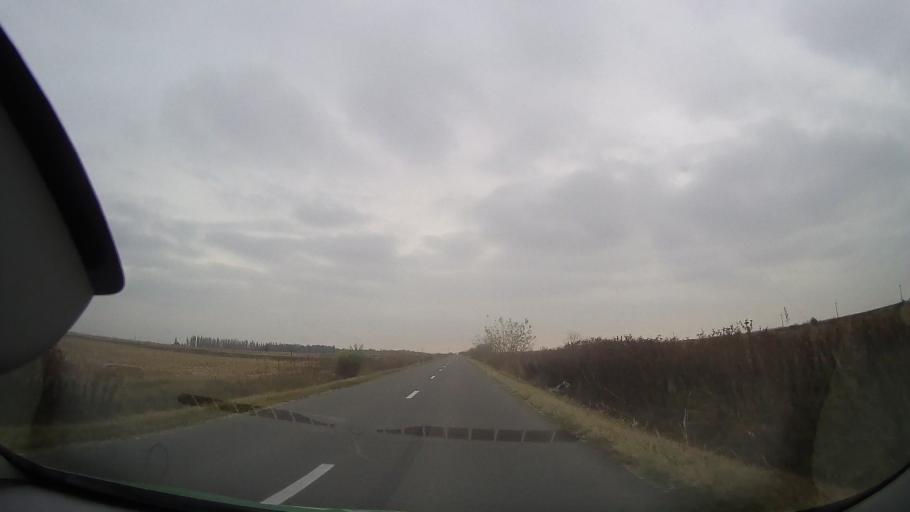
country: RO
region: Ialomita
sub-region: Comuna Alexeni
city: Alexeni
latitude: 44.7433
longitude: 26.7123
